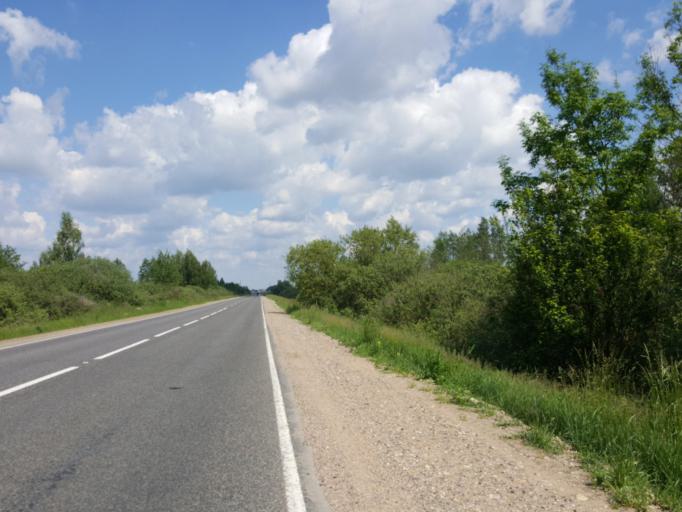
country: BY
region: Brest
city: Kamyanyets
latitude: 52.3881
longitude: 23.7871
